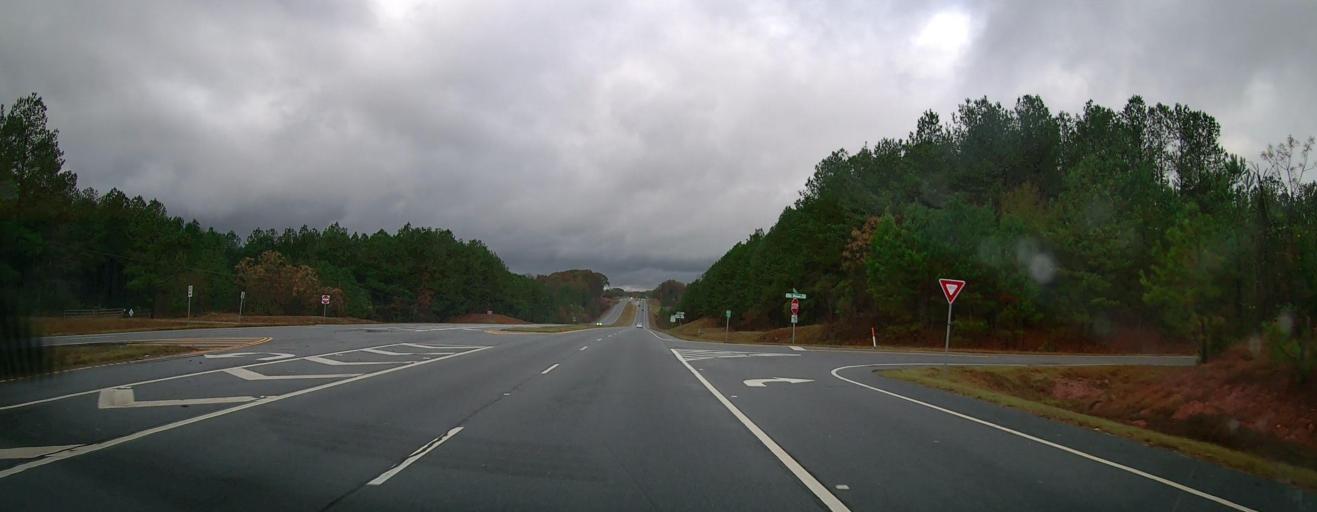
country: US
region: Georgia
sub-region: Jackson County
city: Nicholson
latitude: 34.0861
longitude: -83.4244
